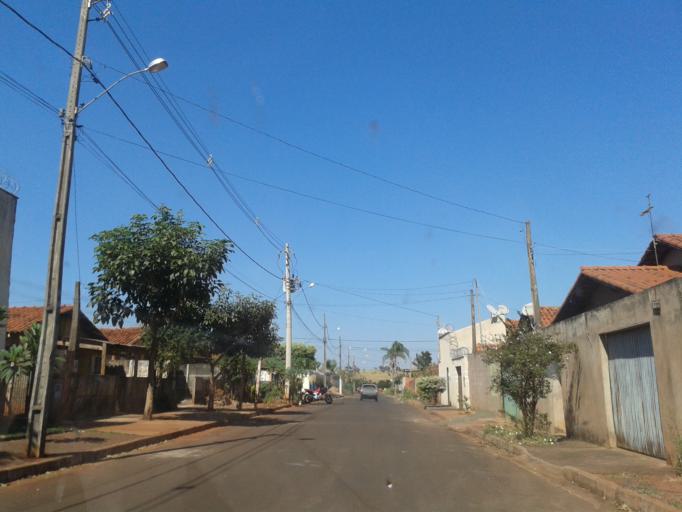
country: BR
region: Minas Gerais
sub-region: Ituiutaba
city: Ituiutaba
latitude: -18.9935
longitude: -49.4605
